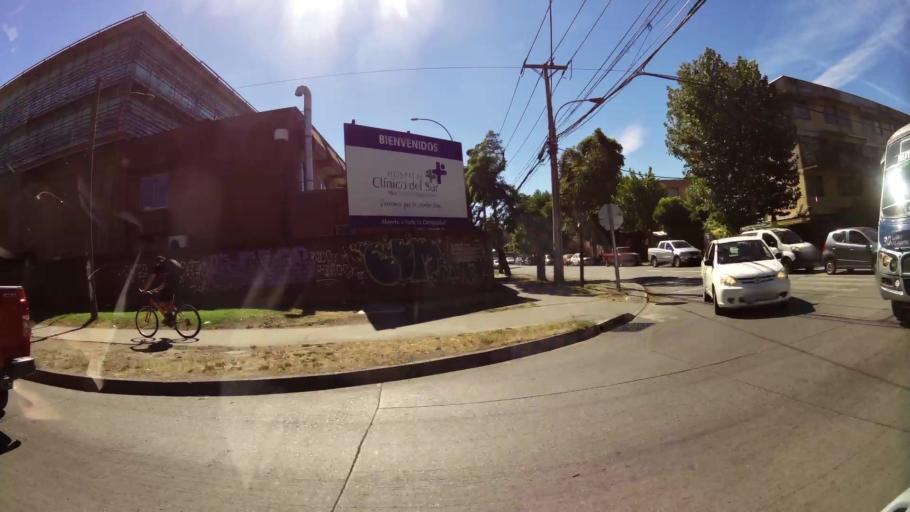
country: CL
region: Biobio
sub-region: Provincia de Concepcion
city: Concepcion
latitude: -36.8137
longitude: -73.0303
